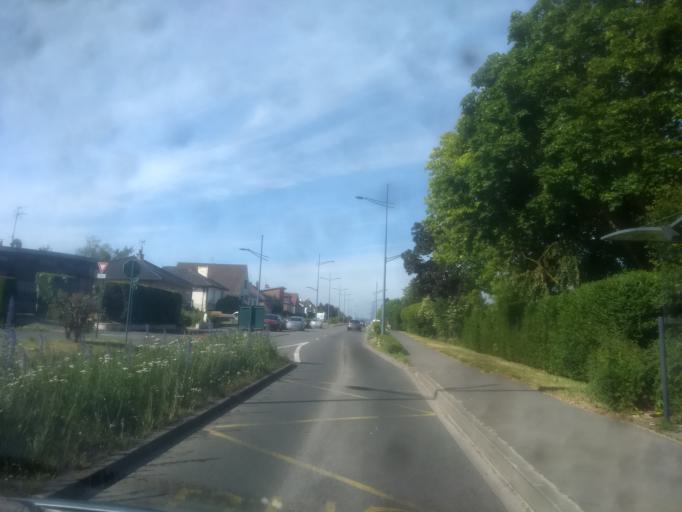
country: FR
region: Nord-Pas-de-Calais
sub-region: Departement du Pas-de-Calais
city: Dainville
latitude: 50.2779
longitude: 2.7273
